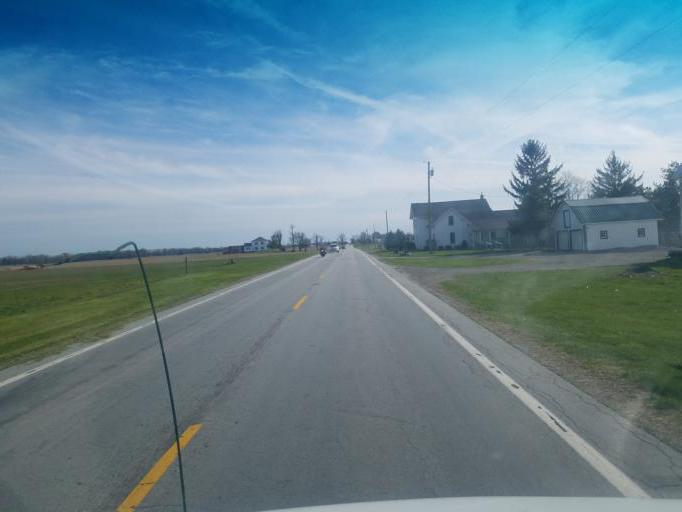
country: US
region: Ohio
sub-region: Union County
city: Richwood
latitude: 40.3677
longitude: -83.2900
